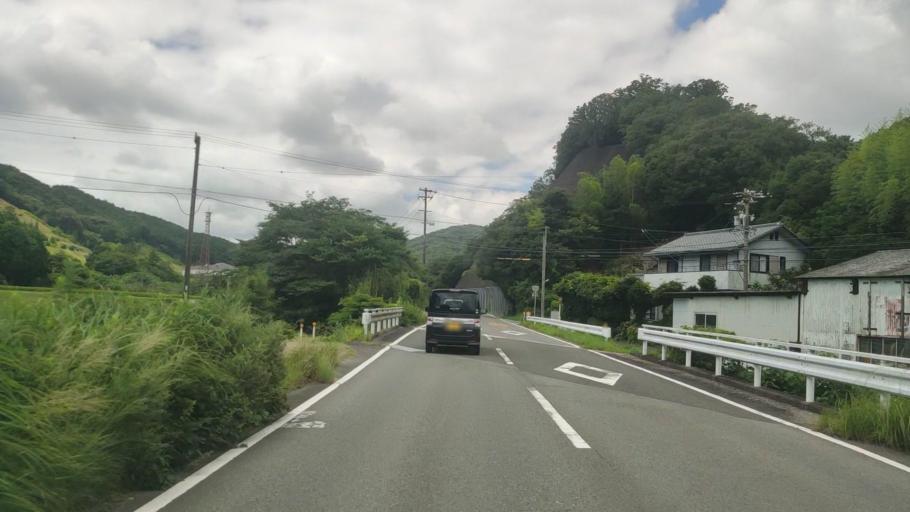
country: JP
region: Mie
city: Toba
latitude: 34.4259
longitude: 136.8233
